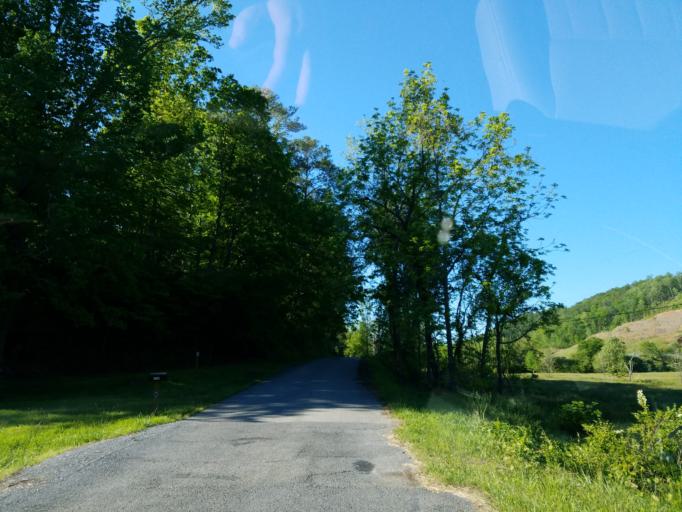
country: US
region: Georgia
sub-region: Gilmer County
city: Ellijay
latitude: 34.5890
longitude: -84.5110
